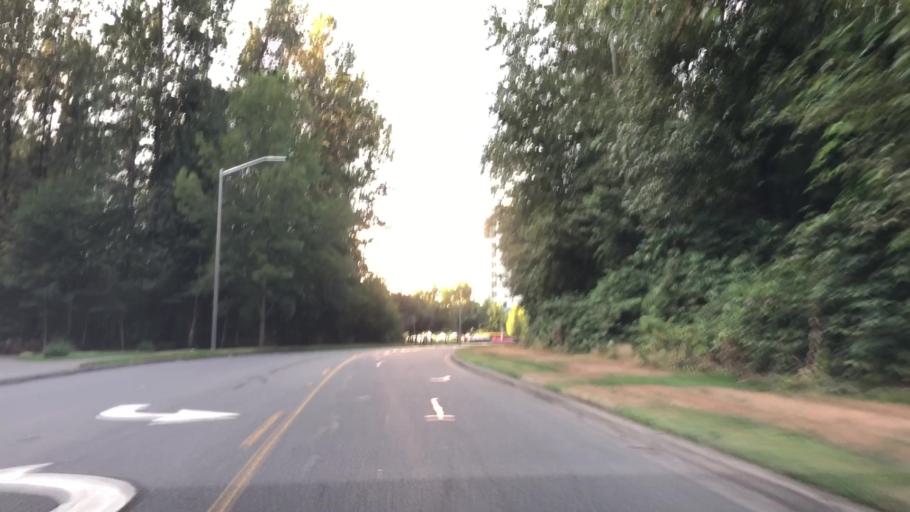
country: US
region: Washington
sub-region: Snohomish County
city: Marysville
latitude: 48.0842
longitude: -122.1891
